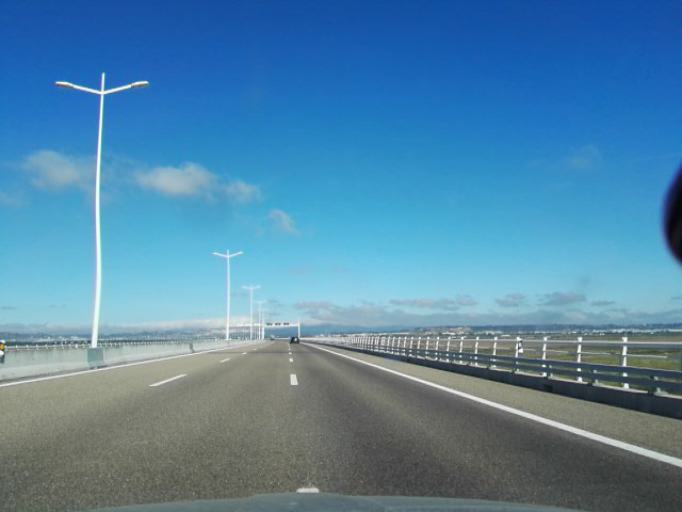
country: PT
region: Santarem
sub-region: Benavente
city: Samora Correia
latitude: 38.9946
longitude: -8.8983
